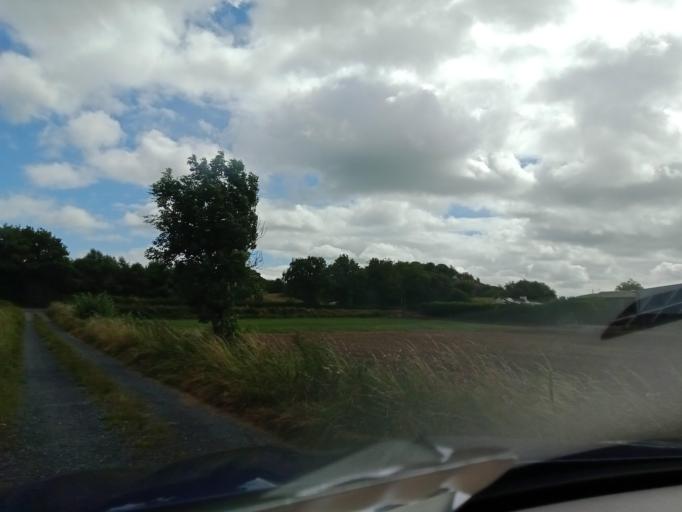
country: IE
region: Leinster
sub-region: Laois
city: Portlaoise
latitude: 52.9820
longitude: -7.2896
